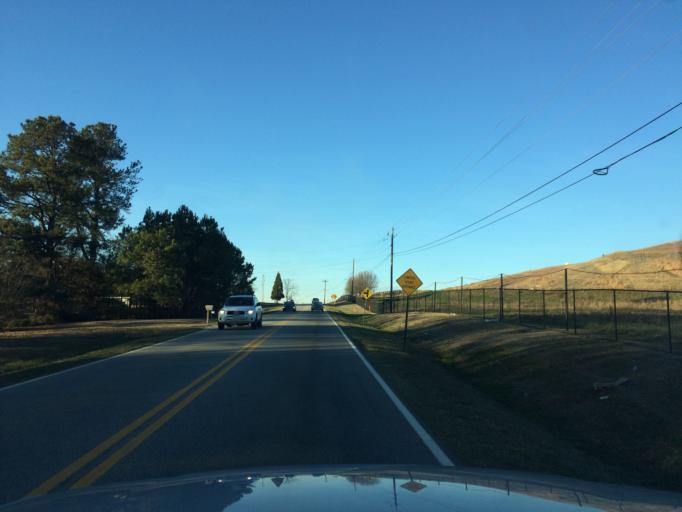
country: US
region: Georgia
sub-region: Barrow County
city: Winder
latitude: 33.9627
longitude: -83.7723
